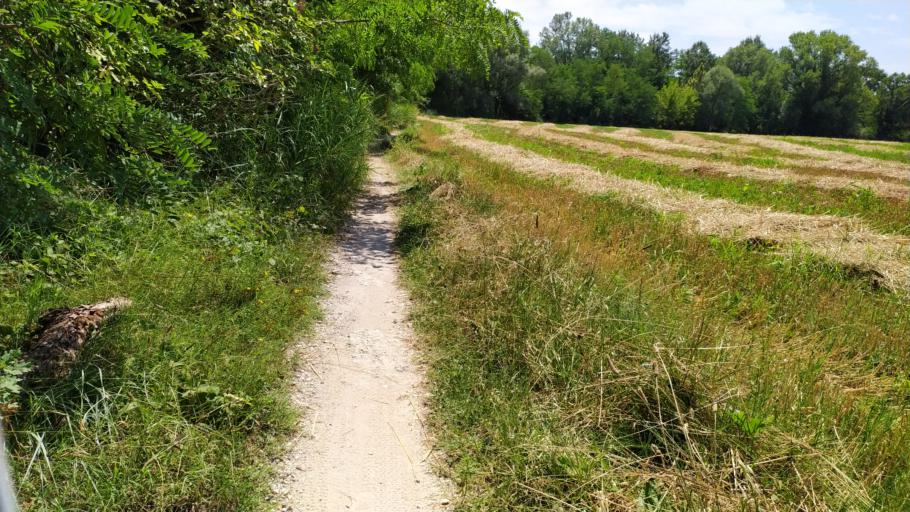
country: IT
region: Emilia-Romagna
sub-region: Forli-Cesena
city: Castrocaro Terme e Terra del Sole
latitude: 44.1905
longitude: 11.9689
